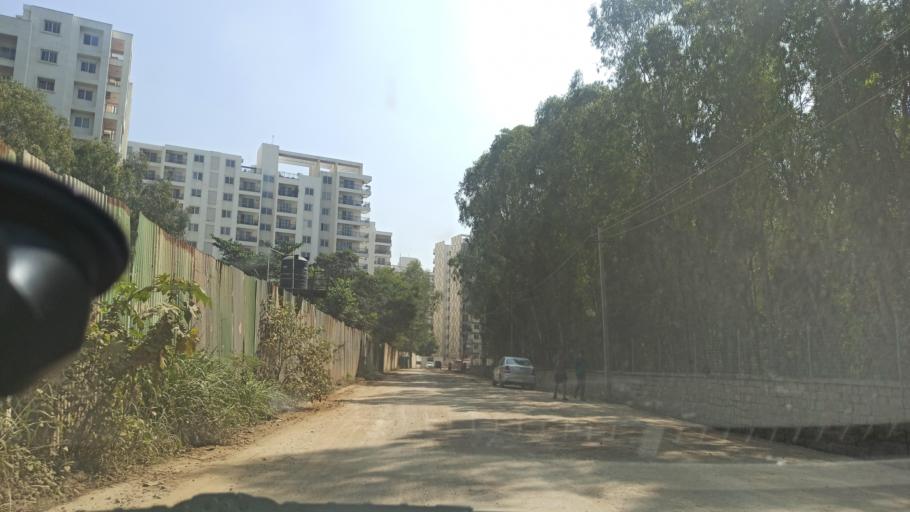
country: IN
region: Karnataka
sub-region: Bangalore Urban
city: Bangalore
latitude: 12.9177
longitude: 77.6879
